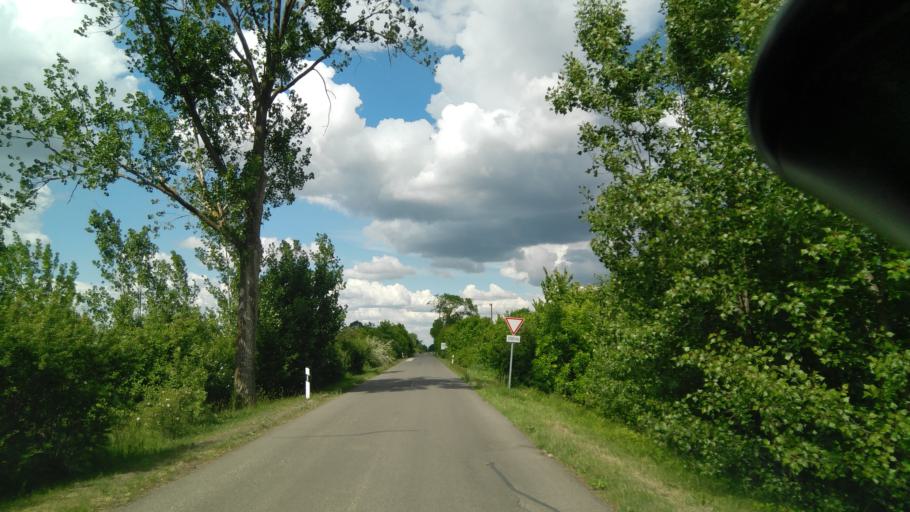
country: HU
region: Bekes
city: Bucsa
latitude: 47.1628
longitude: 21.0868
